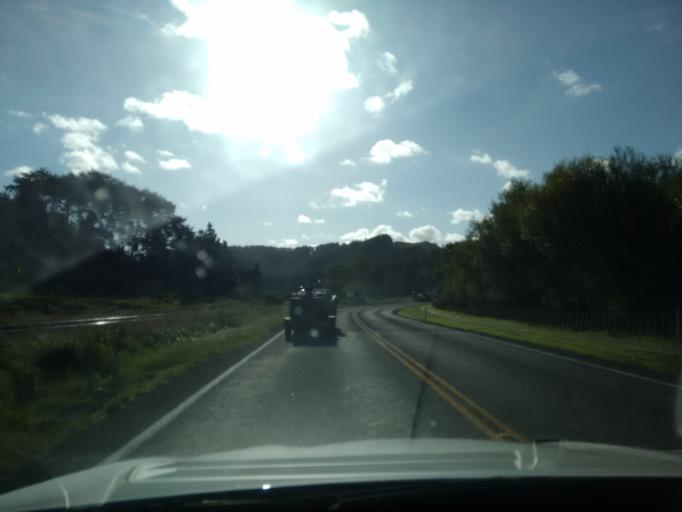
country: NZ
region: Manawatu-Wanganui
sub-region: Wanganui District
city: Wanganui
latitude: -39.8496
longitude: 174.9287
